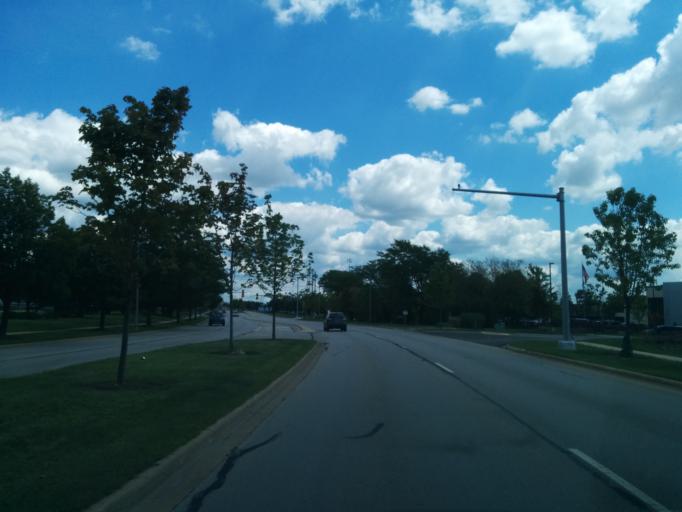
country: US
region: Illinois
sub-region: Will County
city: Romeoville
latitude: 41.6777
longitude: -88.1020
